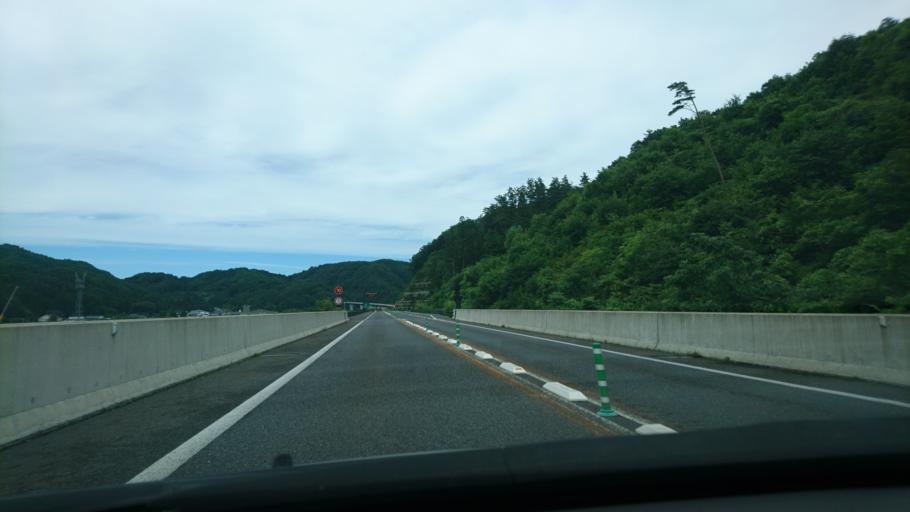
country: JP
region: Iwate
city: Miyako
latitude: 39.9977
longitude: 141.8851
